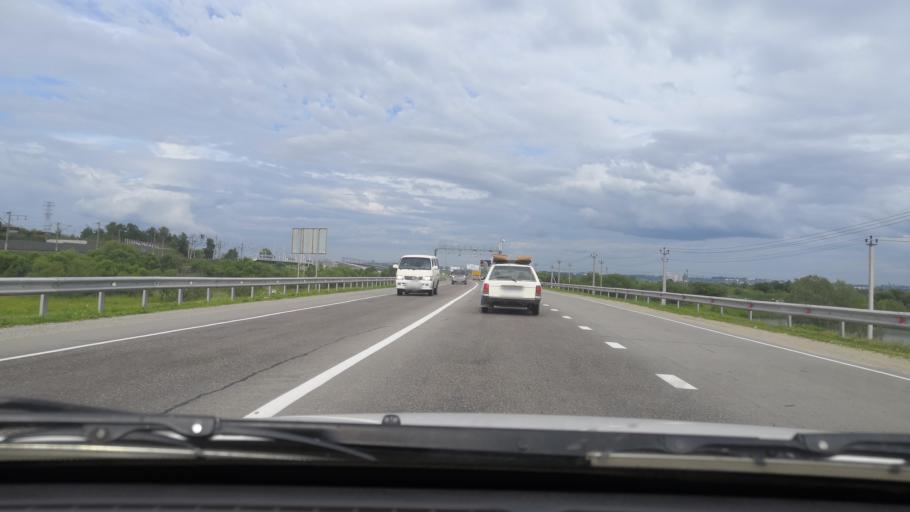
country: RU
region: Jewish Autonomous Oblast
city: Priamurskiy
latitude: 48.5272
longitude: 134.9550
